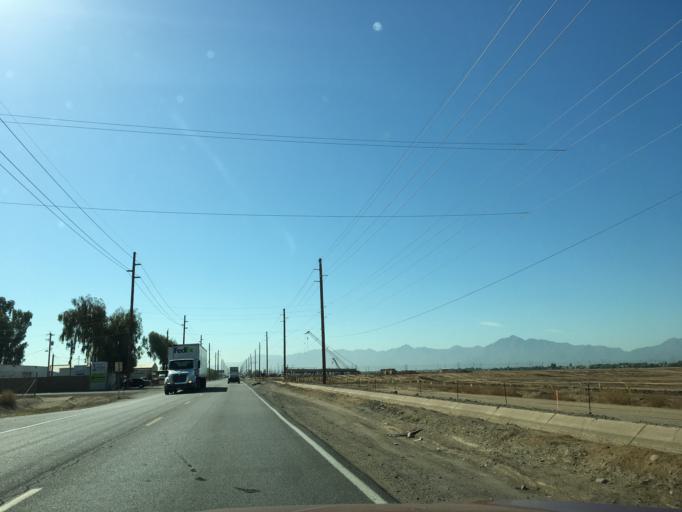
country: US
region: Arizona
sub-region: Maricopa County
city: Laveen
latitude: 33.4345
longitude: -112.1866
